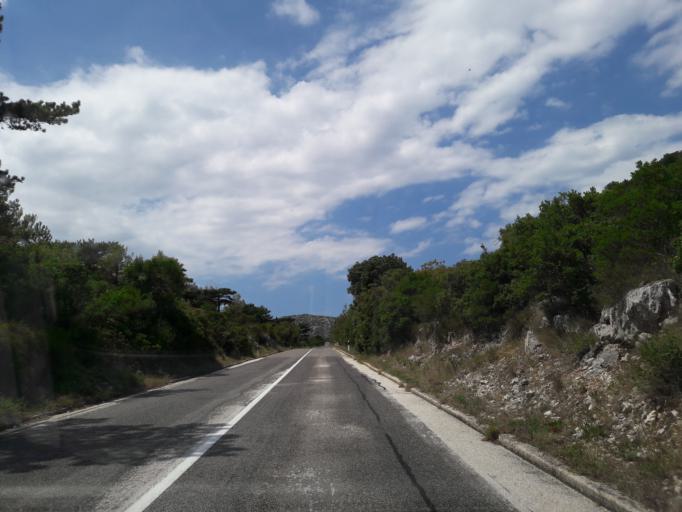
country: HR
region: Dubrovacko-Neretvanska
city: Orebic
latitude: 42.9701
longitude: 17.2798
